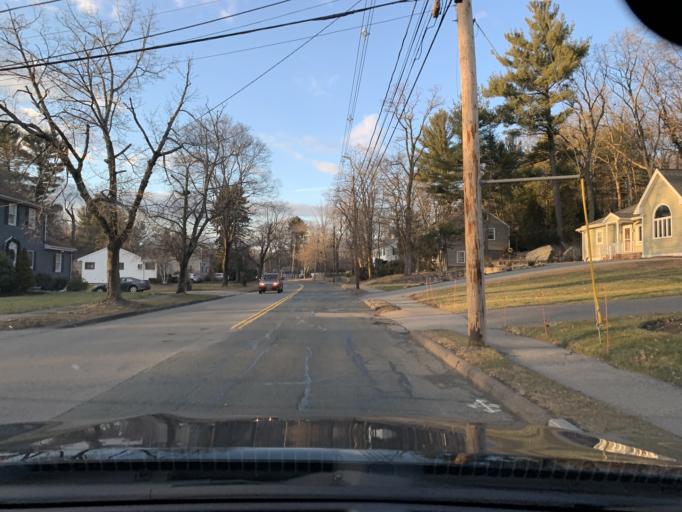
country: US
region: Massachusetts
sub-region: Essex County
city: Lynnfield
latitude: 42.5193
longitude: -71.0158
